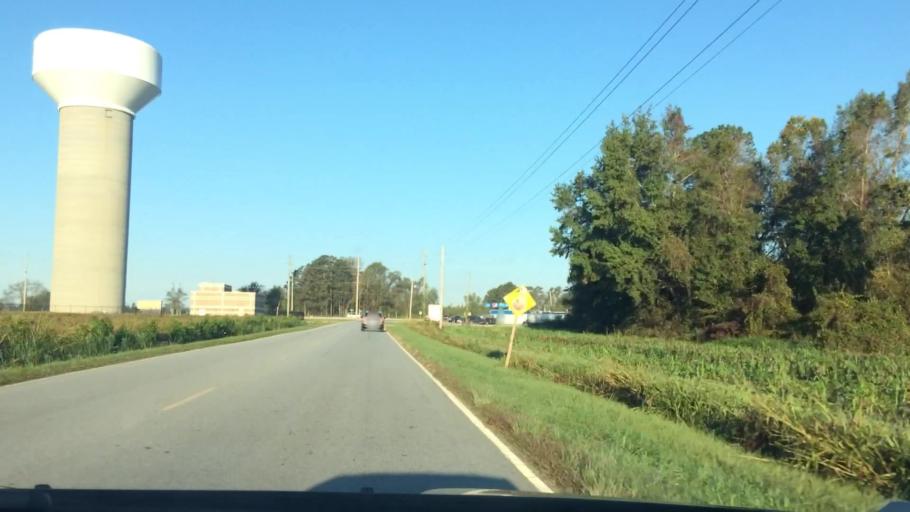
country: US
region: North Carolina
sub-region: Pitt County
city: Grifton
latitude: 35.4088
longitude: -77.4323
